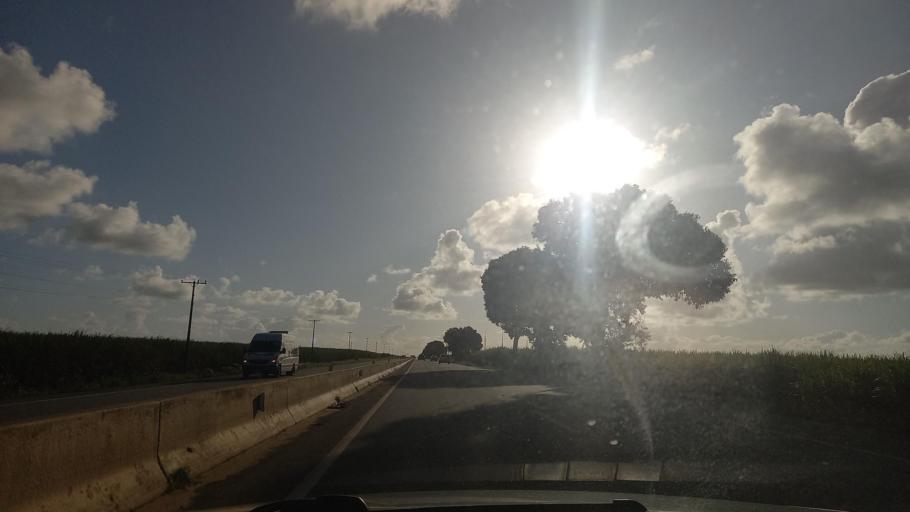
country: BR
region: Alagoas
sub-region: Sao Miguel Dos Campos
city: Sao Miguel dos Campos
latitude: -9.8057
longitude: -36.1233
